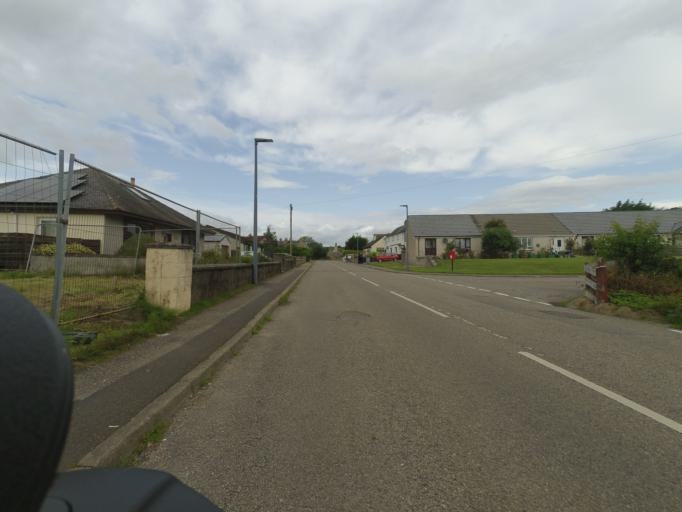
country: GB
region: Scotland
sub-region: Highland
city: Dornoch
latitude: 57.8777
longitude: -4.0268
